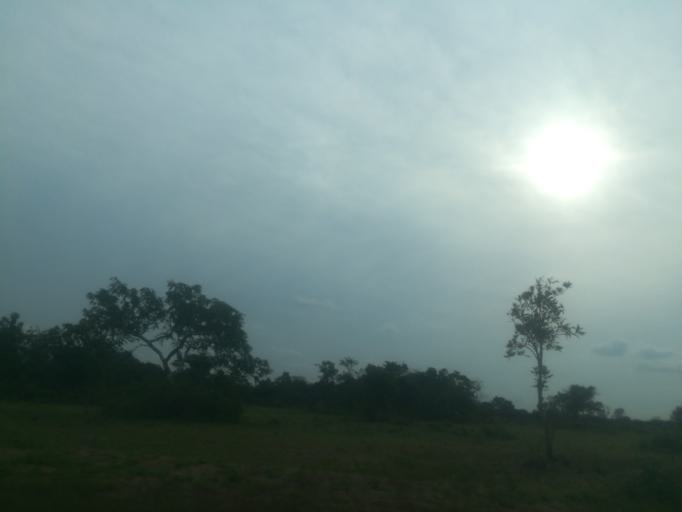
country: NG
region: Ogun
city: Ayetoro
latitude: 7.2727
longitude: 3.1009
